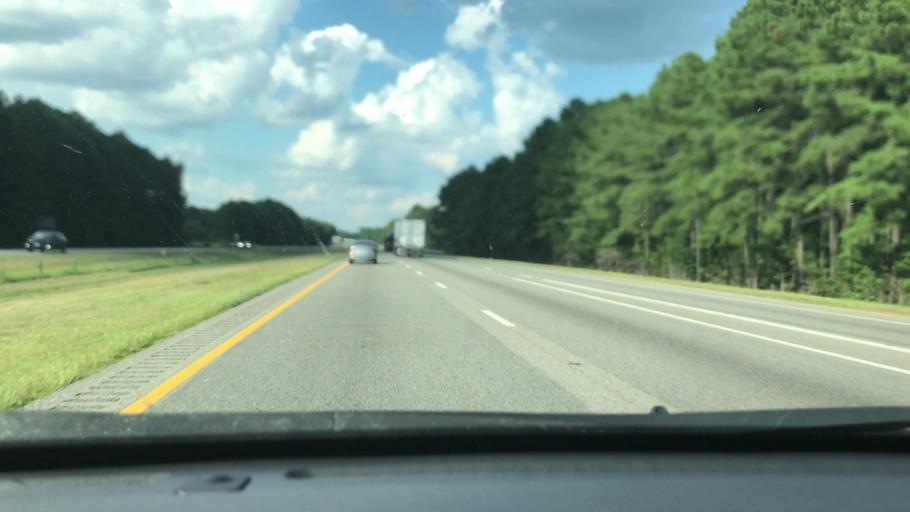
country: US
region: South Carolina
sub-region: Florence County
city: Timmonsville
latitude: 33.9504
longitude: -80.0531
